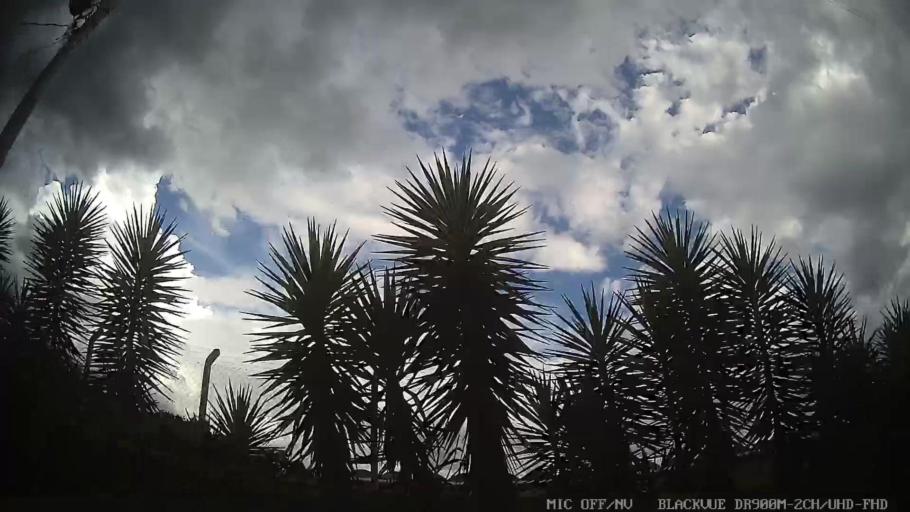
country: BR
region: Sao Paulo
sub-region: Jaguariuna
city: Jaguariuna
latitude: -22.6484
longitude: -47.0638
